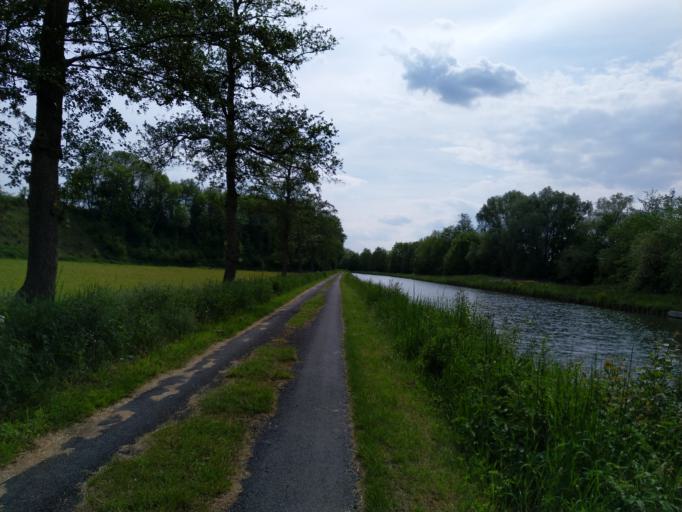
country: FR
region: Picardie
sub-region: Departement de l'Aisne
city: Etreux
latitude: 49.9875
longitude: 3.6459
